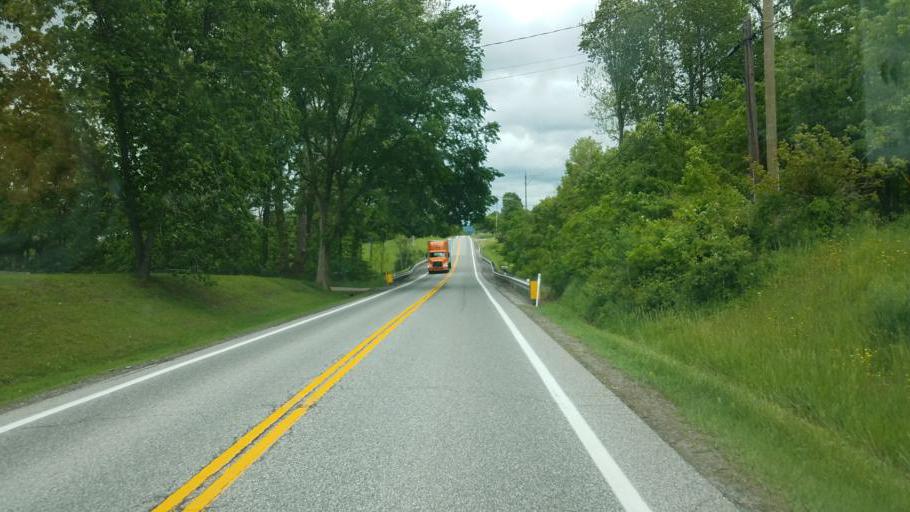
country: US
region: Ohio
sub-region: Geauga County
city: Middlefield
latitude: 41.3889
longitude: -81.0320
